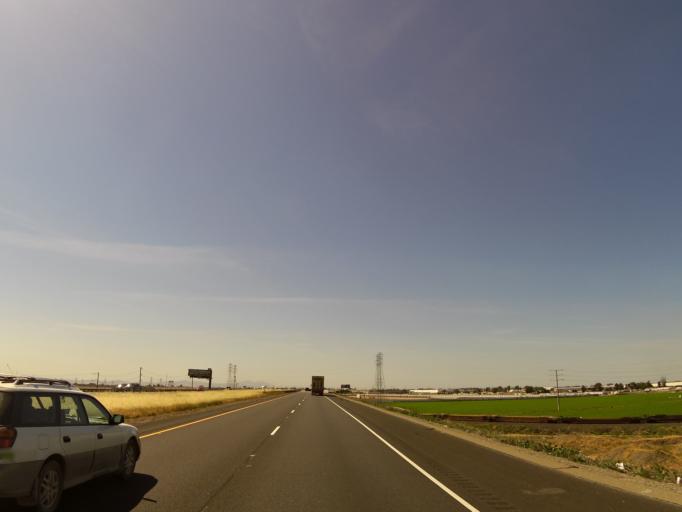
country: US
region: California
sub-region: San Joaquin County
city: Lathrop
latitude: 37.7864
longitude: -121.2757
